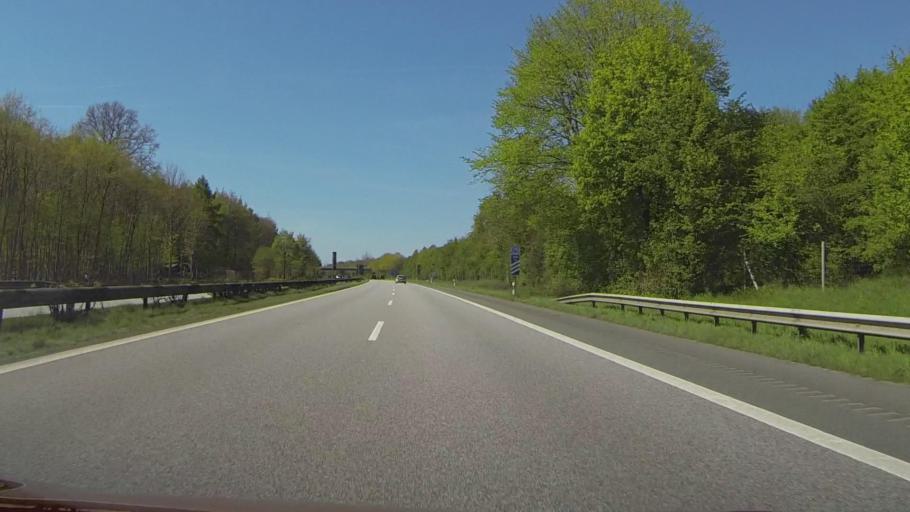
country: DE
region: Schleswig-Holstein
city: Ellerhoop
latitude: 53.7103
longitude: 9.7663
